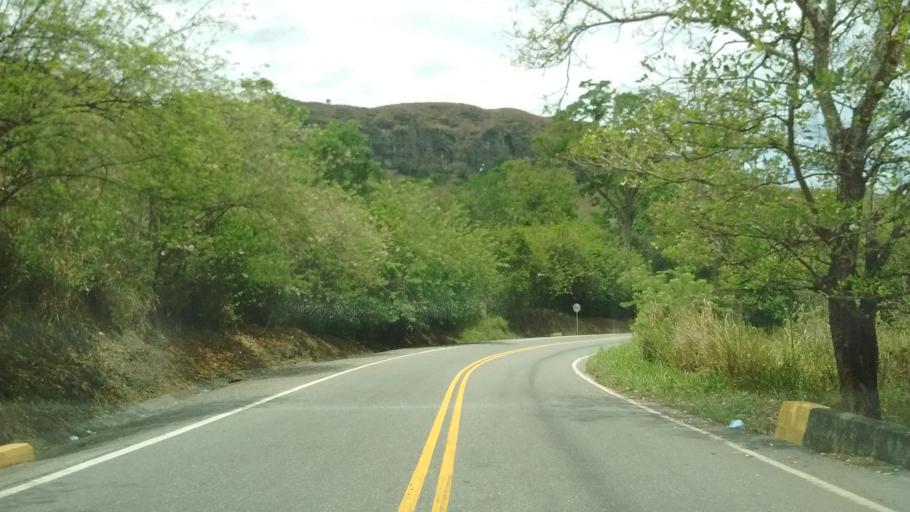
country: CO
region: Cauca
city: La Sierra
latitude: 2.2060
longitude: -76.8097
